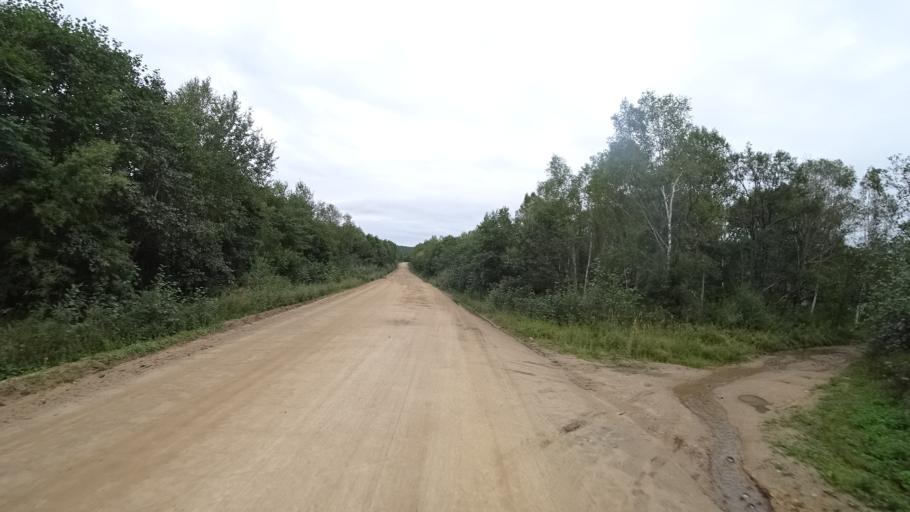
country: RU
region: Primorskiy
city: Rettikhovka
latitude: 44.1765
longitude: 132.8022
